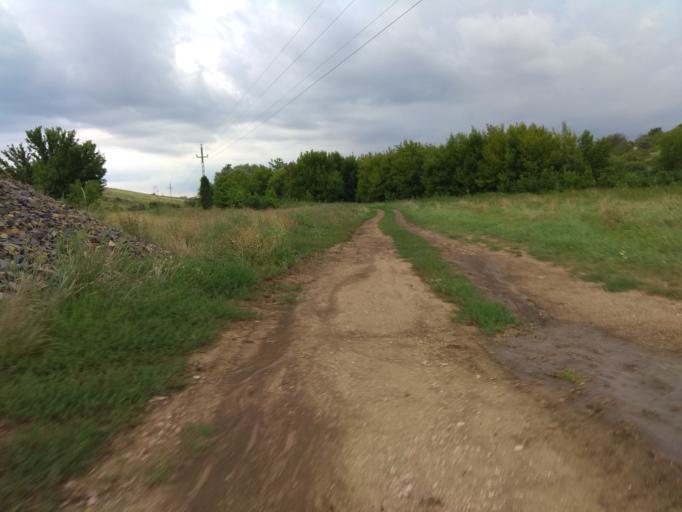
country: HU
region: Borsod-Abauj-Zemplen
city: Monok
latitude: 48.1846
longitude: 21.1257
